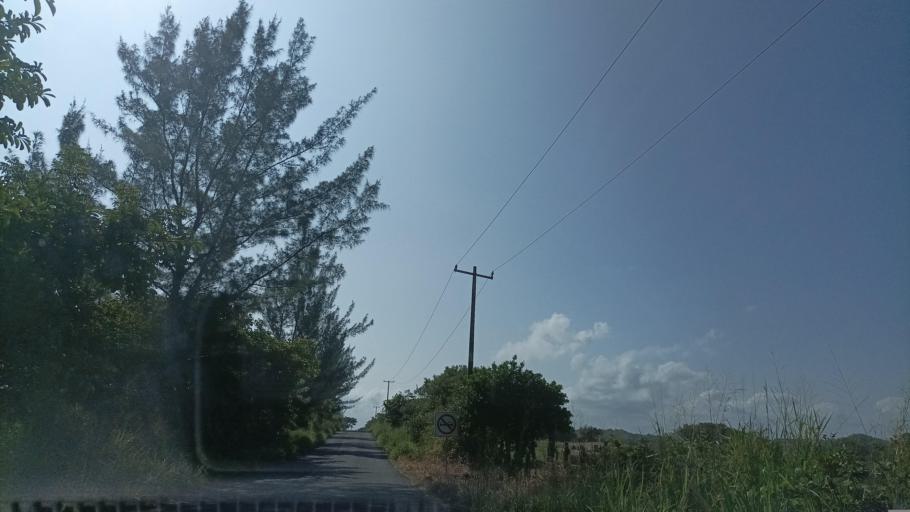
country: MX
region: Veracruz
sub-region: Pajapan
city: Pajapan
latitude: 18.2394
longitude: -94.6210
